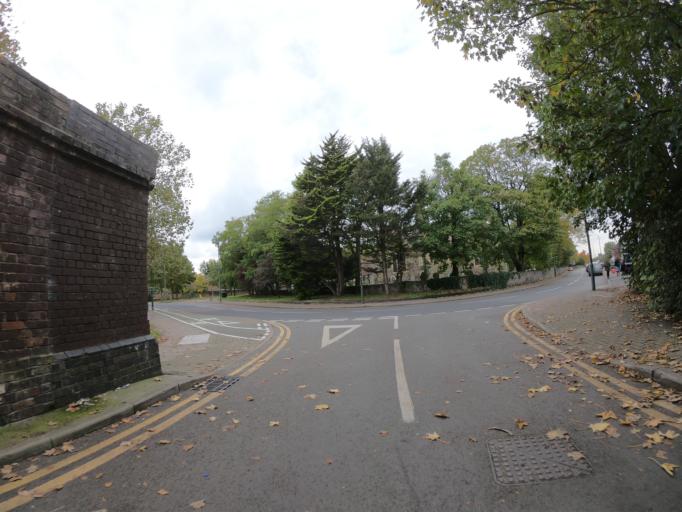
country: GB
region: England
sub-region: Greater London
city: Erith
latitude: 51.4874
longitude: 0.1710
